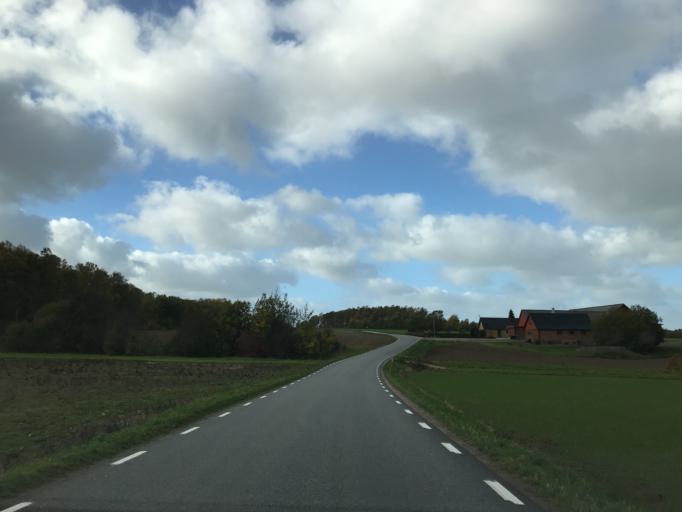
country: SE
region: Skane
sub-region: Bjuvs Kommun
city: Billesholm
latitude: 56.0117
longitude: 12.9853
